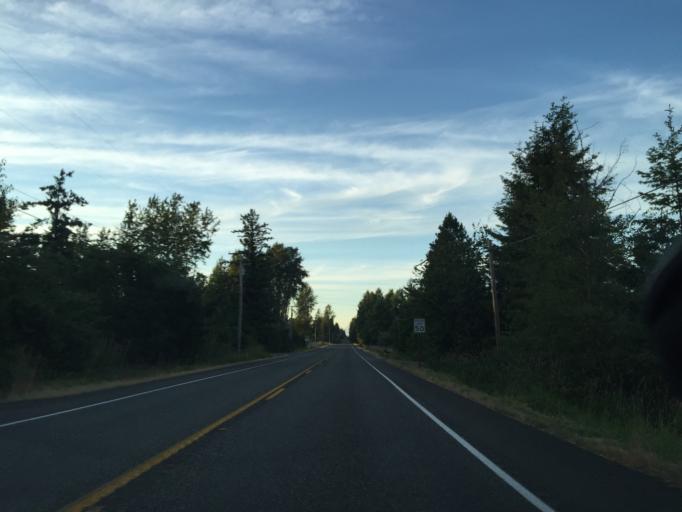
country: US
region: Washington
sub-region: Whatcom County
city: Geneva
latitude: 48.8189
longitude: -122.3770
